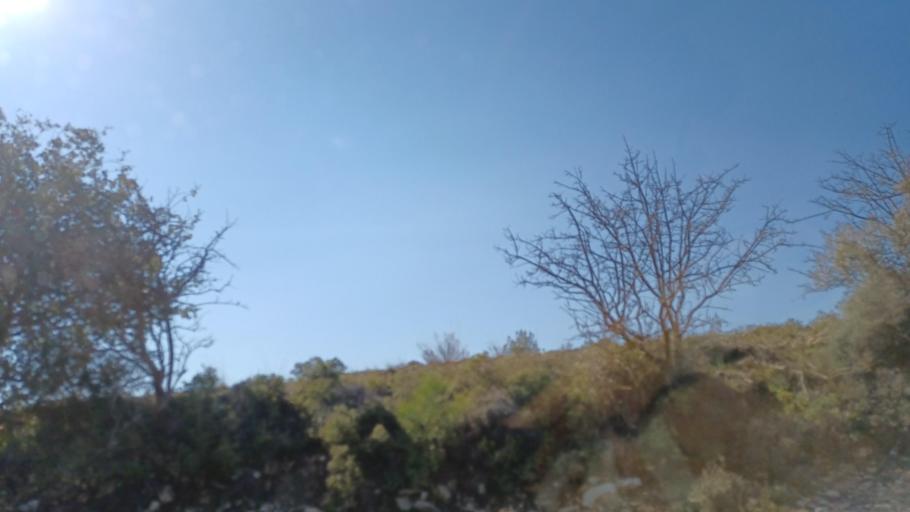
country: CY
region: Limassol
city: Pachna
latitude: 34.8487
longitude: 32.6902
